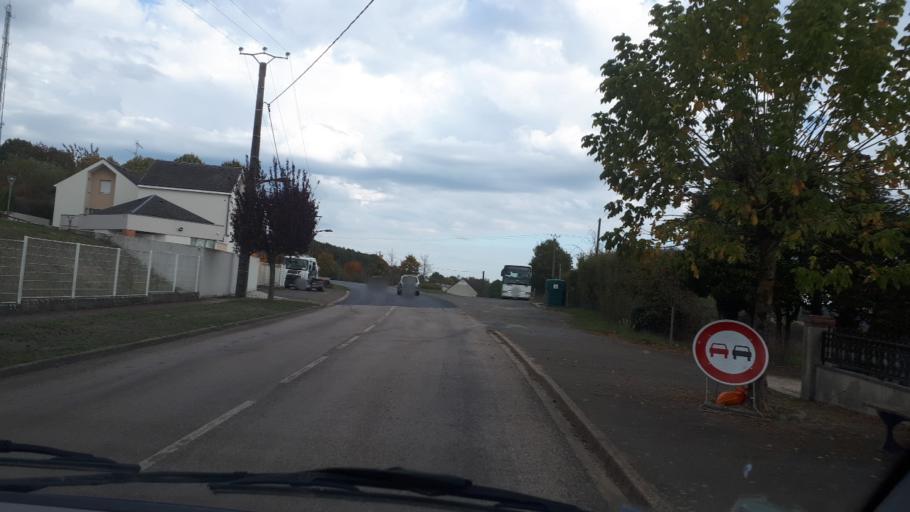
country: FR
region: Centre
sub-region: Departement d'Eure-et-Loir
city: Authon-du-Perche
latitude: 48.2001
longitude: 0.8937
